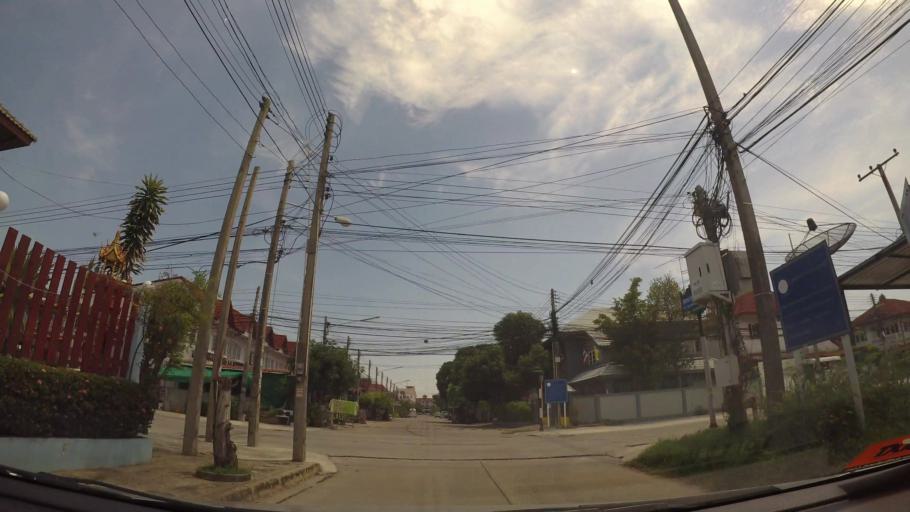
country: TH
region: Chon Buri
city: Chon Buri
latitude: 13.3343
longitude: 100.9483
